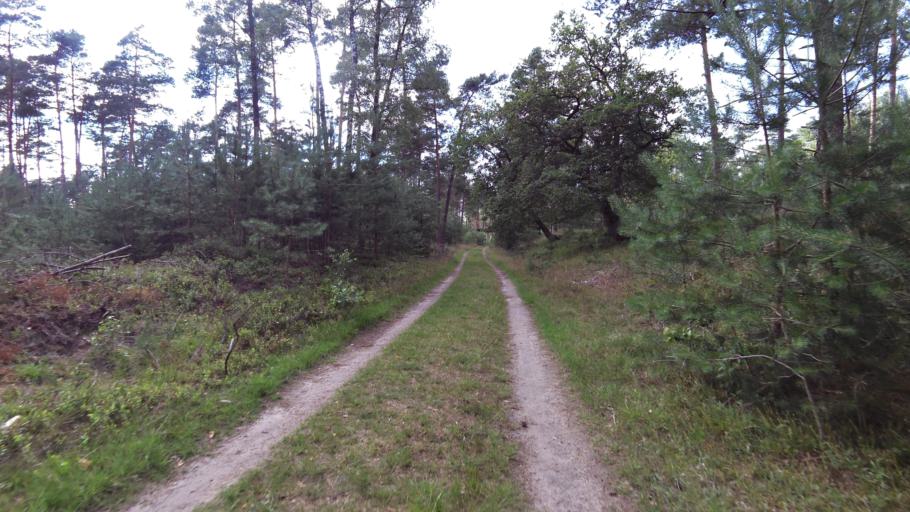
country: NL
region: Gelderland
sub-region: Gemeente Epe
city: Vaassen
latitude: 52.2847
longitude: 5.8921
